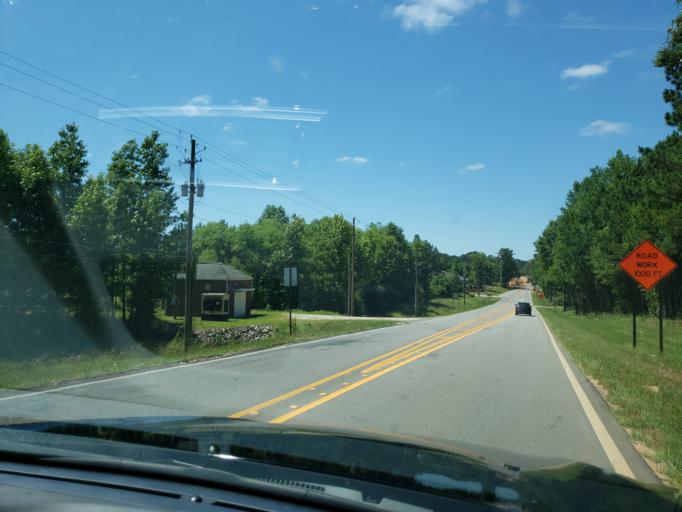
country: US
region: Alabama
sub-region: Lee County
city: Auburn
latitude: 32.6707
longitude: -85.4882
